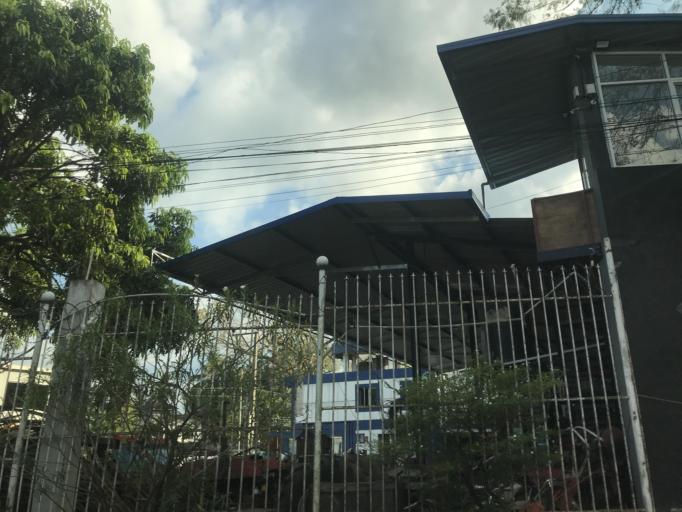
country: LK
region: Western
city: Gampaha
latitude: 7.0640
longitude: 80.0107
